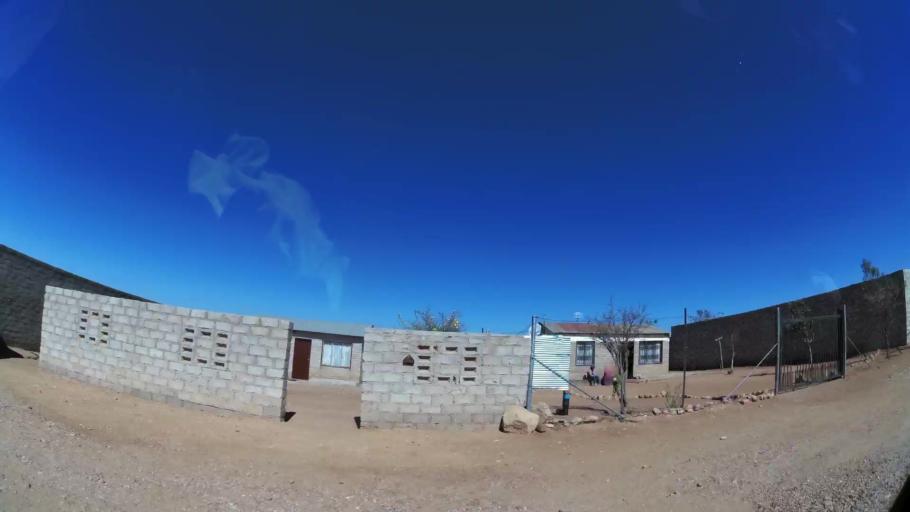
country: ZA
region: Limpopo
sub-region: Capricorn District Municipality
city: Polokwane
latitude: -23.8813
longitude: 29.4088
